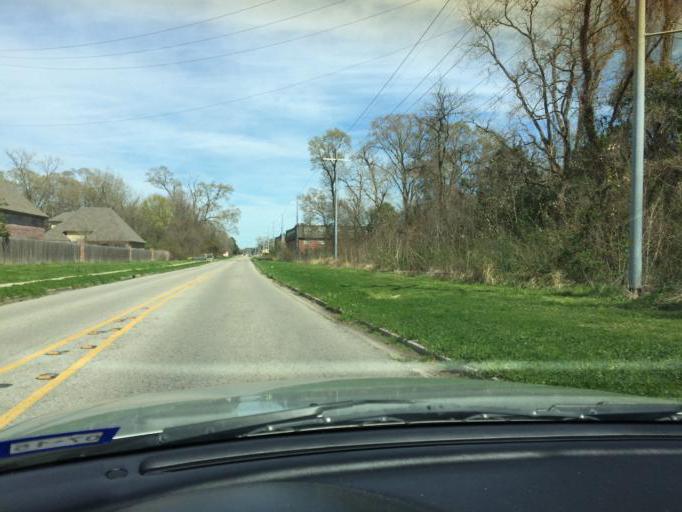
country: US
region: Louisiana
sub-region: Lafayette Parish
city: Scott
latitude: 30.2152
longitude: -92.0621
